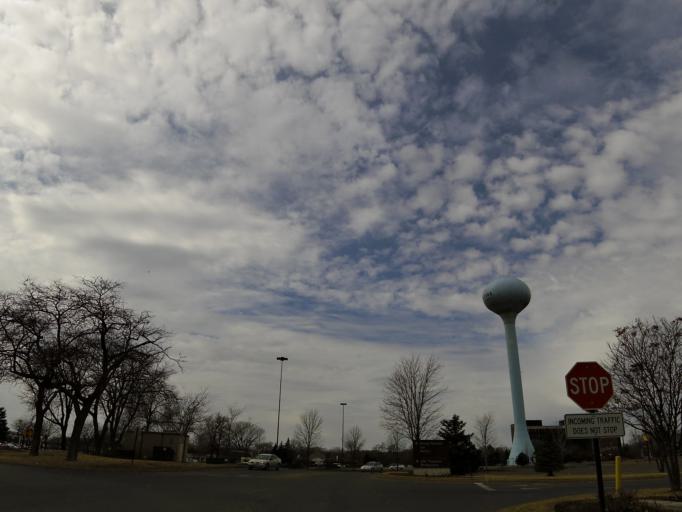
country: US
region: Minnesota
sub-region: Hennepin County
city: Edina
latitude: 44.8786
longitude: -93.3263
